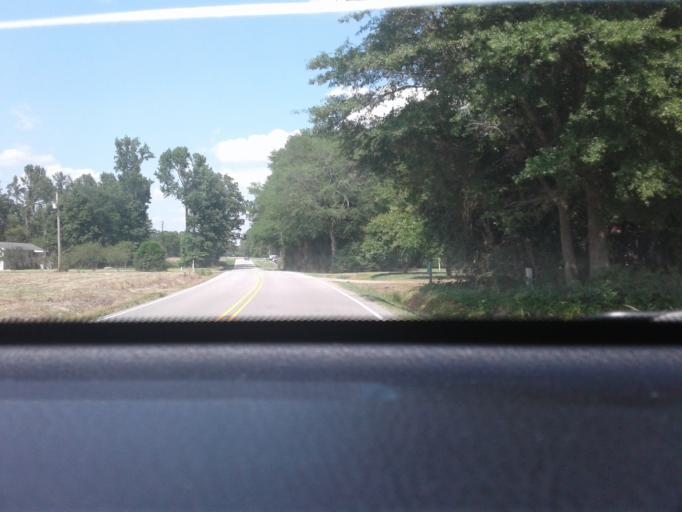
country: US
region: North Carolina
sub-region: Harnett County
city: Erwin
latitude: 35.2238
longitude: -78.6861
